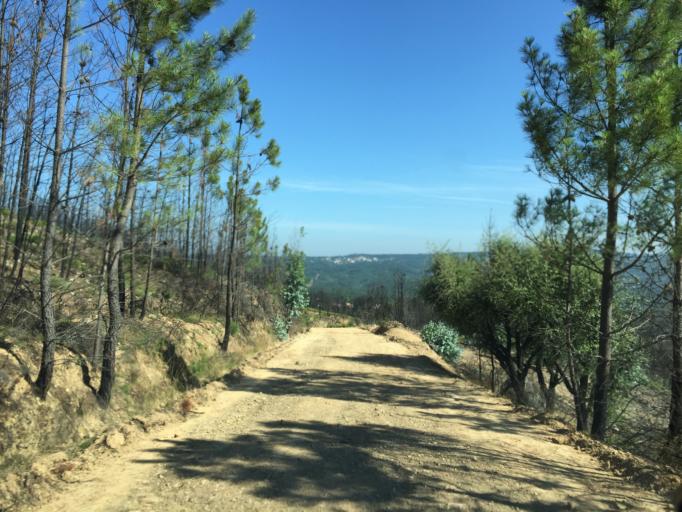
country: PT
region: Santarem
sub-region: Macao
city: Macao
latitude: 39.6586
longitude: -7.9850
